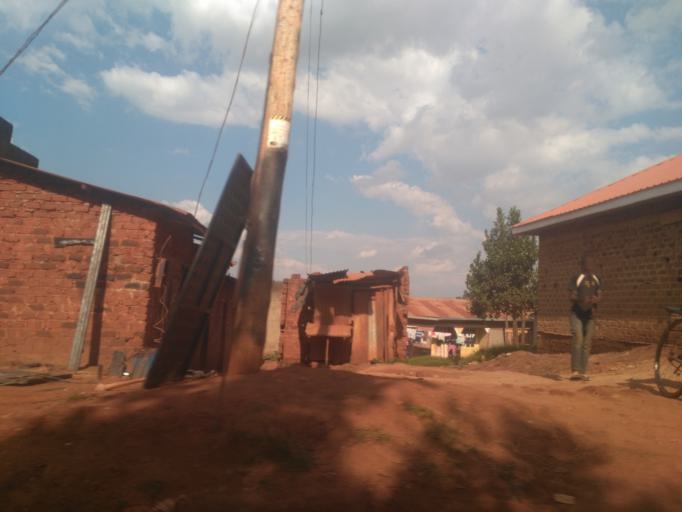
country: UG
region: Central Region
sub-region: Wakiso District
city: Kajansi
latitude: 0.2642
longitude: 32.4383
